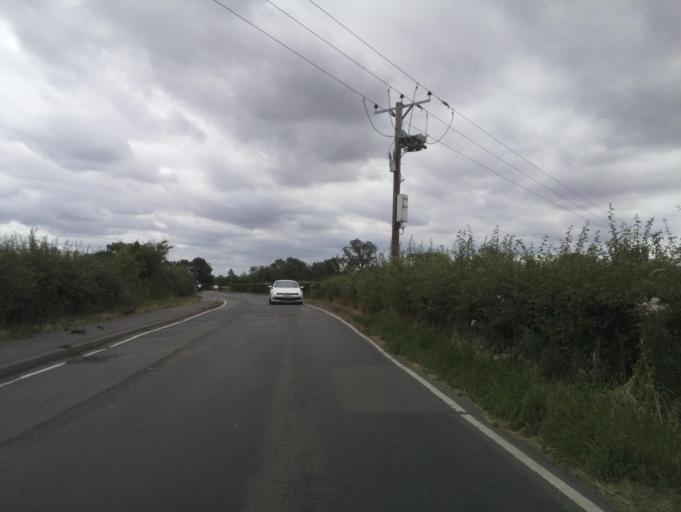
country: GB
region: England
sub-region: Derbyshire
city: Long Eaton
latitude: 52.9074
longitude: -1.3193
